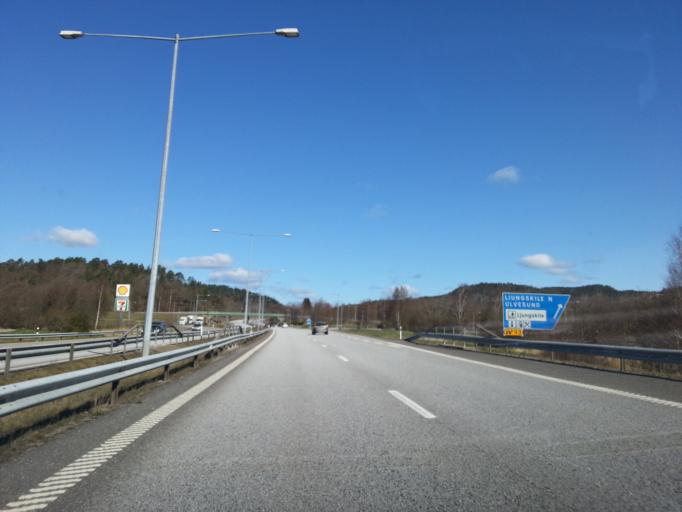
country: SE
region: Vaestra Goetaland
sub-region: Uddevalla Kommun
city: Ljungskile
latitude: 58.2282
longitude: 11.9160
